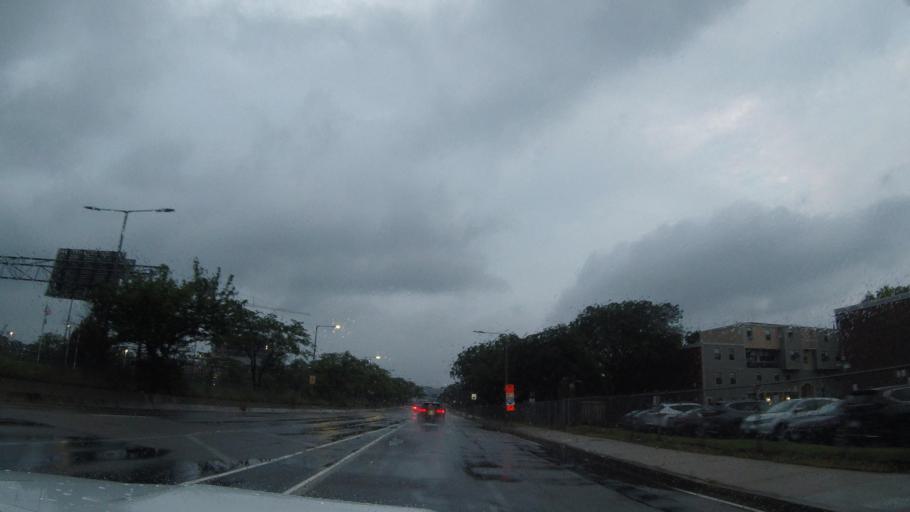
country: US
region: Massachusetts
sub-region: Suffolk County
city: Boston
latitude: 42.3762
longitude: -71.0688
